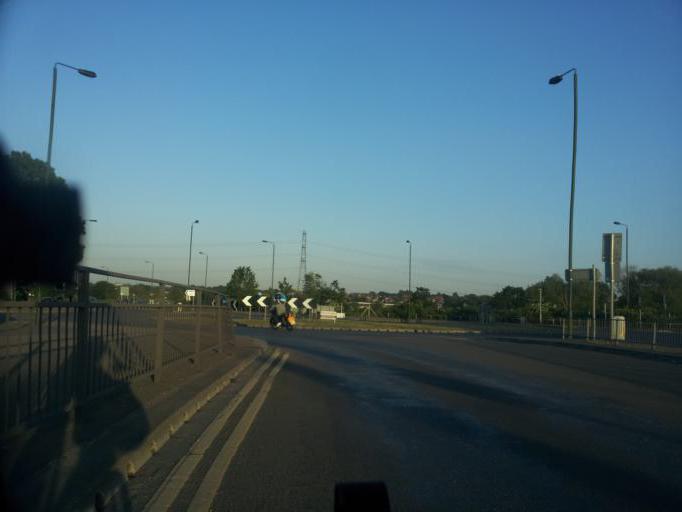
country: GB
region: England
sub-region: Kent
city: Dartford
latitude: 51.4568
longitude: 0.1958
